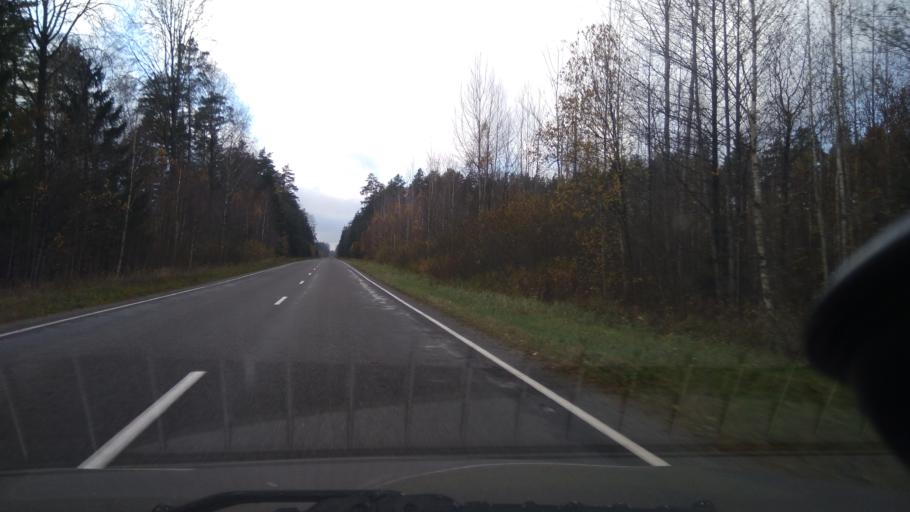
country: BY
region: Minsk
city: Urechcha
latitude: 53.2089
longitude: 27.9586
